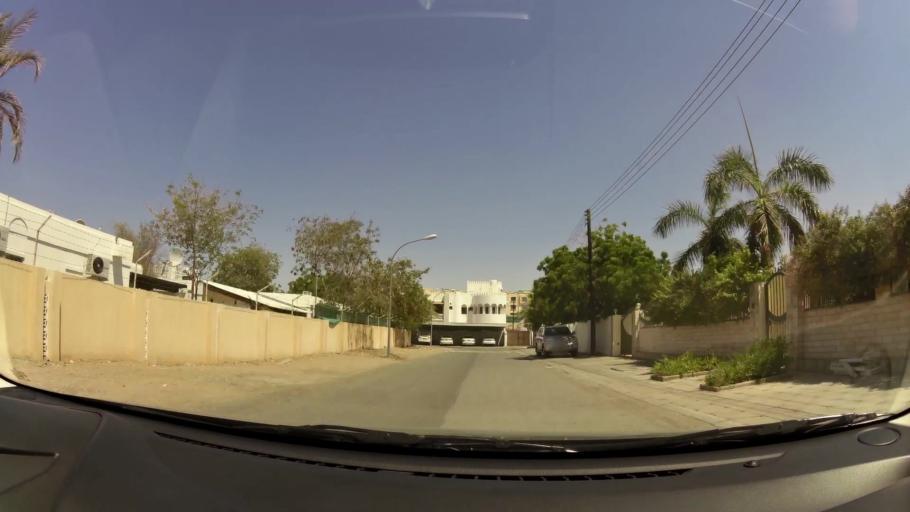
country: OM
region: Muhafazat Masqat
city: As Sib al Jadidah
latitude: 23.6300
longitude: 58.2308
